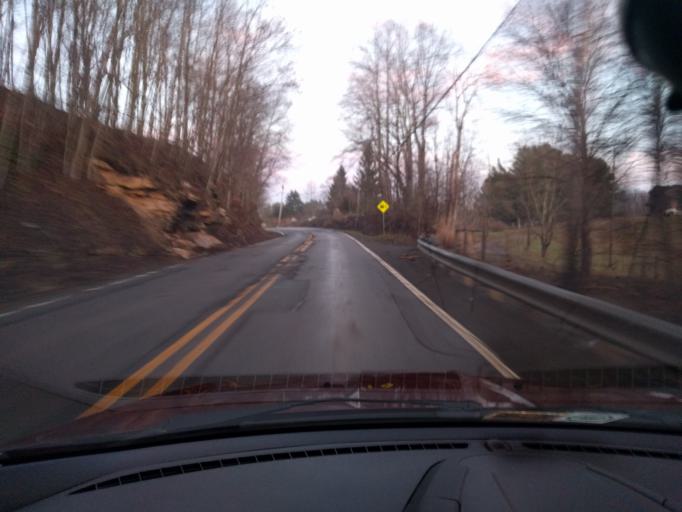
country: US
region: West Virginia
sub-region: Greenbrier County
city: Rainelle
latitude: 38.0108
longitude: -80.8817
